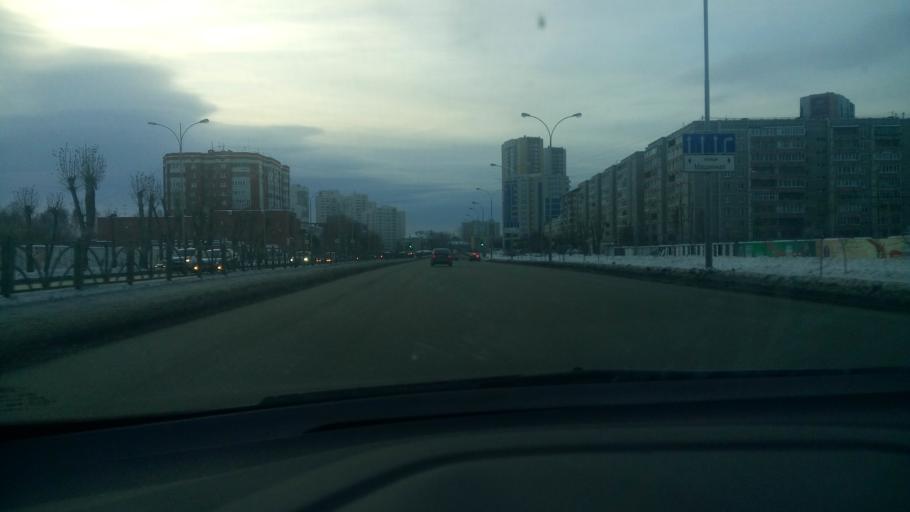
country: RU
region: Sverdlovsk
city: Yekaterinburg
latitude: 56.8092
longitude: 60.6303
